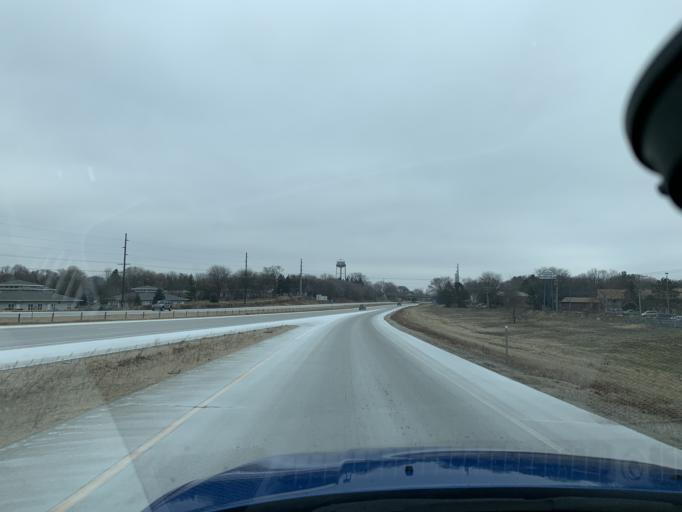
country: US
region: Wisconsin
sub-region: Dane County
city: Sun Prairie
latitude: 43.1889
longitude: -89.2309
